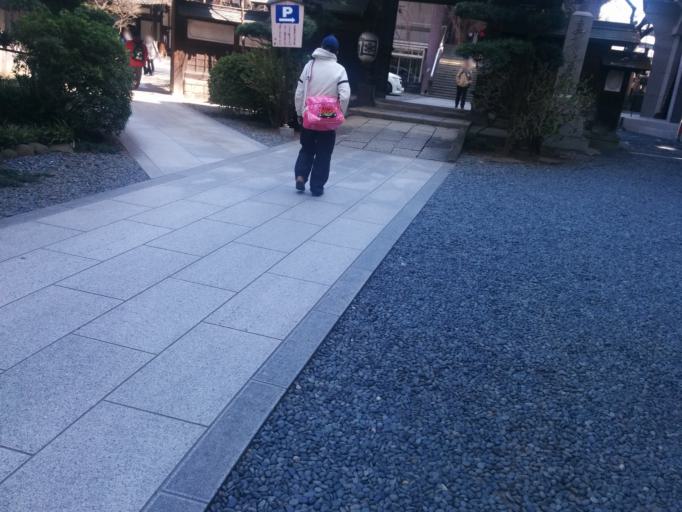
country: JP
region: Tokyo
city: Tokyo
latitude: 35.6936
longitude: 139.6962
